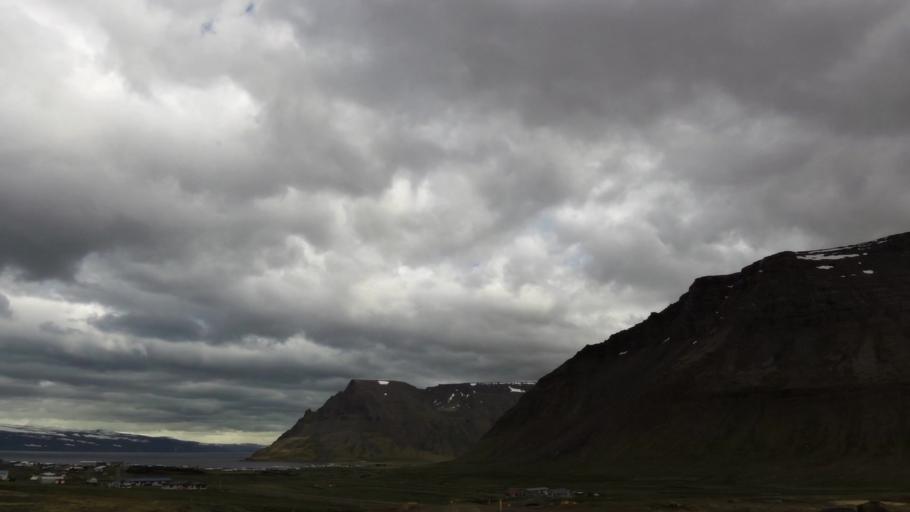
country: IS
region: Westfjords
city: Isafjoerdur
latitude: 66.1588
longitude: -23.2955
